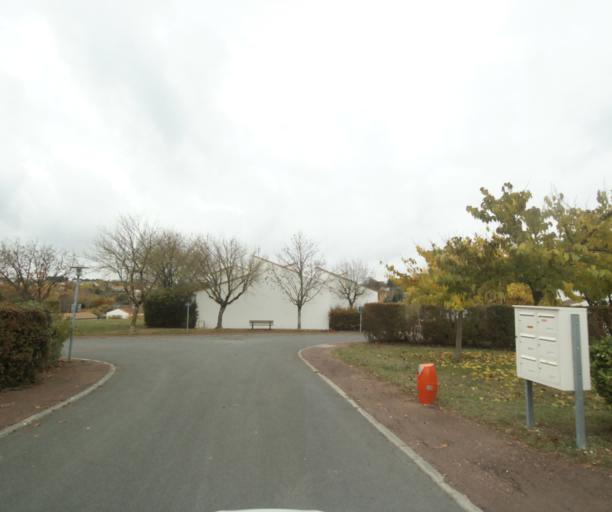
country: FR
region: Poitou-Charentes
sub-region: Departement de la Charente-Maritime
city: Saintes
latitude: 45.7394
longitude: -0.6479
